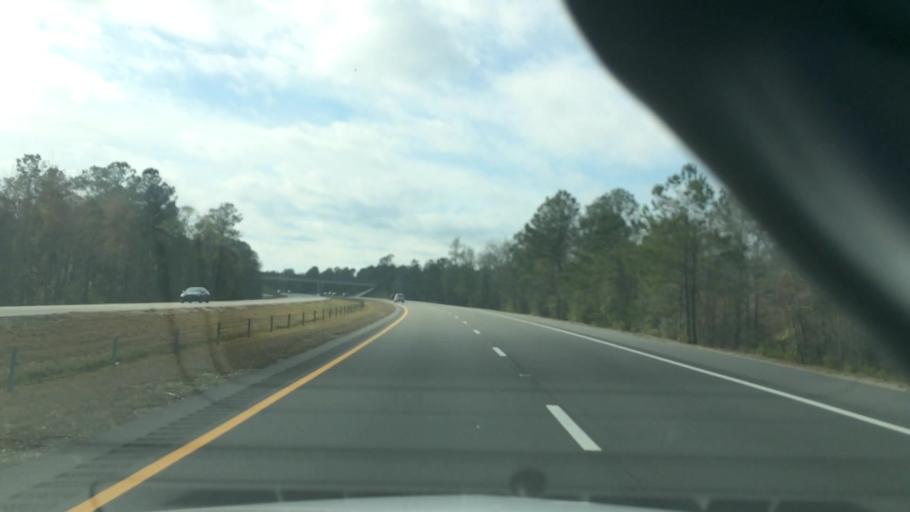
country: US
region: North Carolina
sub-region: New Hanover County
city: Wrightsboro
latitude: 34.3187
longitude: -77.9394
